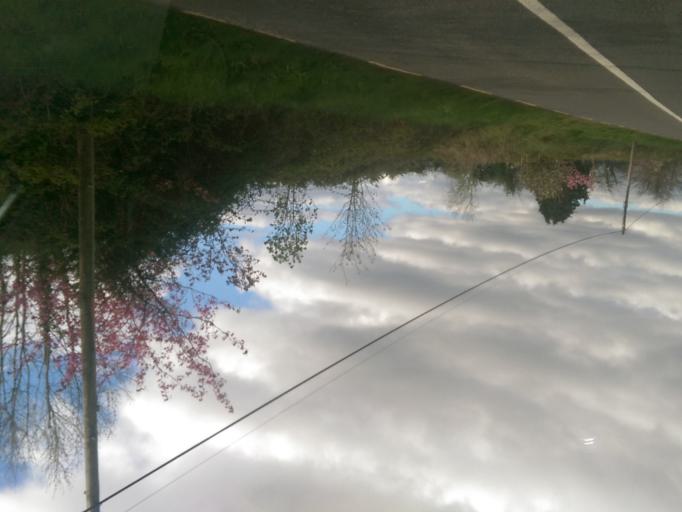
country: IE
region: Connaught
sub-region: County Galway
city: Ballinasloe
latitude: 53.4243
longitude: -8.4040
